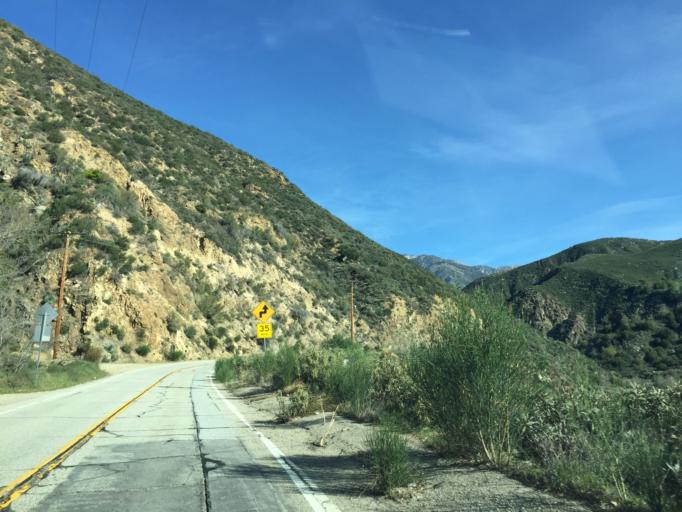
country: US
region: California
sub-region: San Bernardino County
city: San Antonio Heights
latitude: 34.1975
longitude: -117.6770
